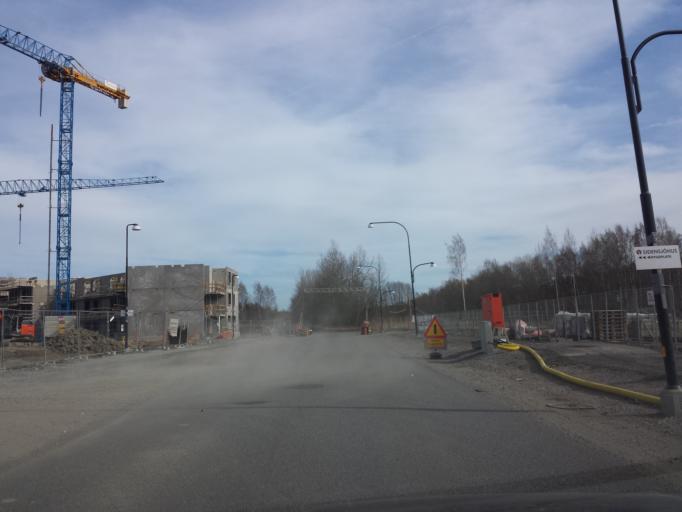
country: SE
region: OErebro
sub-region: Orebro Kommun
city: Orebro
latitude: 59.2521
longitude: 15.2207
